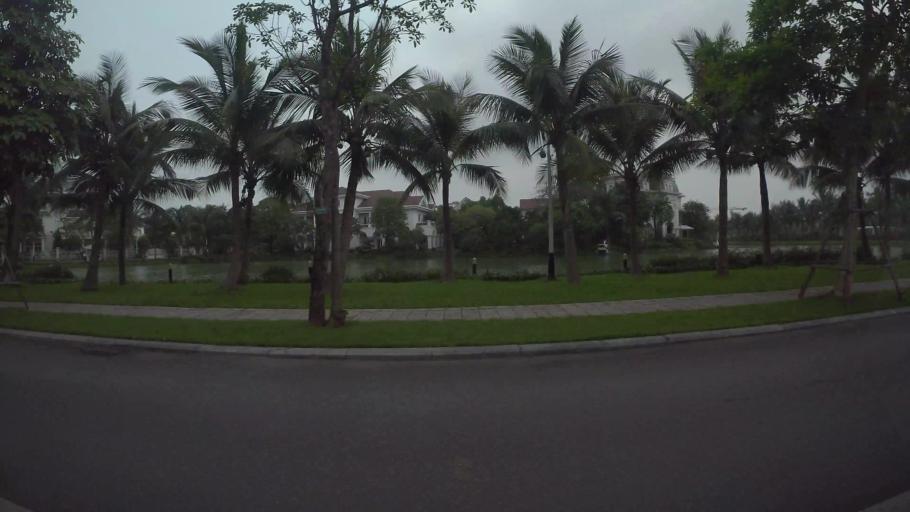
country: VN
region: Ha Noi
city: Trau Quy
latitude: 21.0488
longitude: 105.9121
